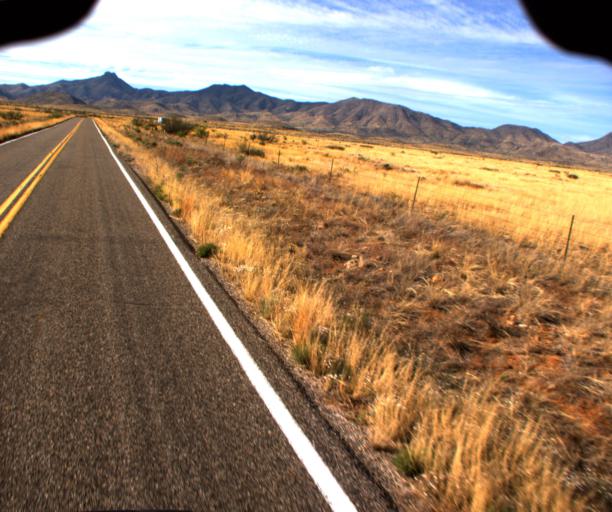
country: US
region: Arizona
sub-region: Cochise County
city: Willcox
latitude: 32.1113
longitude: -109.5494
